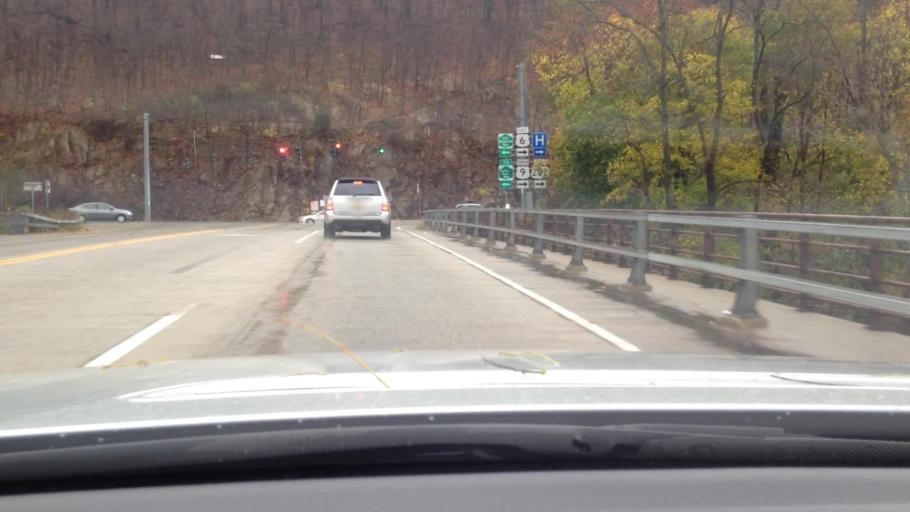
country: US
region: New York
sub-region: Westchester County
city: Peekskill
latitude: 41.2965
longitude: -73.9340
